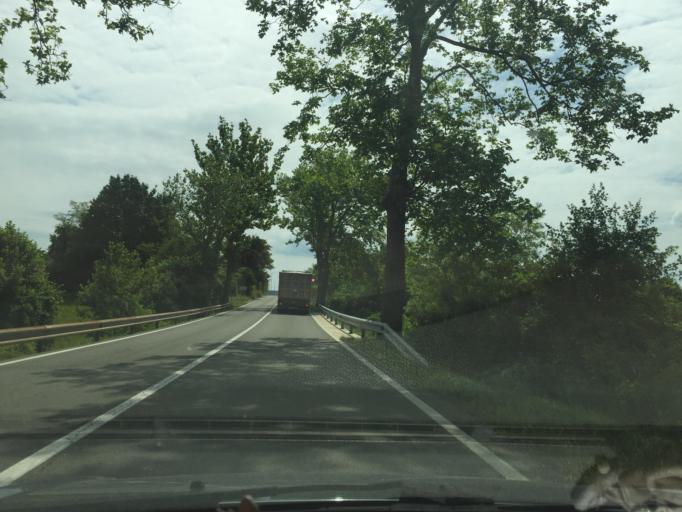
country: SI
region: Hrpelje-Kozina
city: Kozina
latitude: 45.5960
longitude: 13.9690
